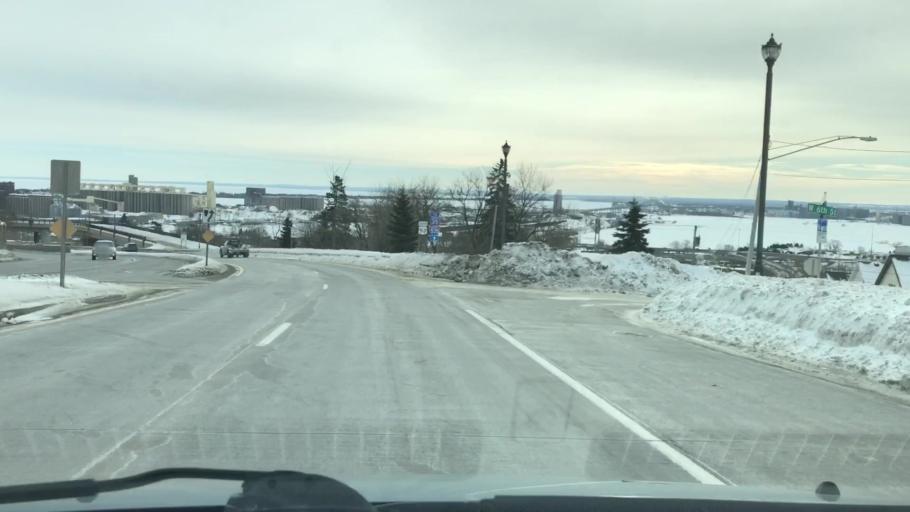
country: US
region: Minnesota
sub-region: Saint Louis County
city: Duluth
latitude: 46.7711
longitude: -92.1308
